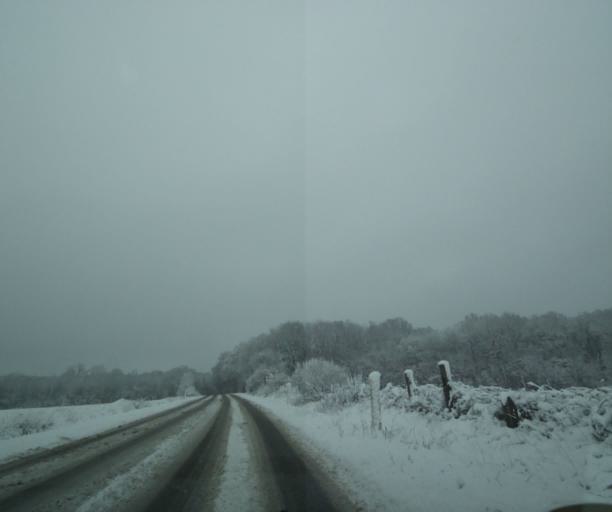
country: FR
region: Champagne-Ardenne
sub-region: Departement de la Haute-Marne
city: Saint-Dizier
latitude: 48.5992
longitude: 4.9096
